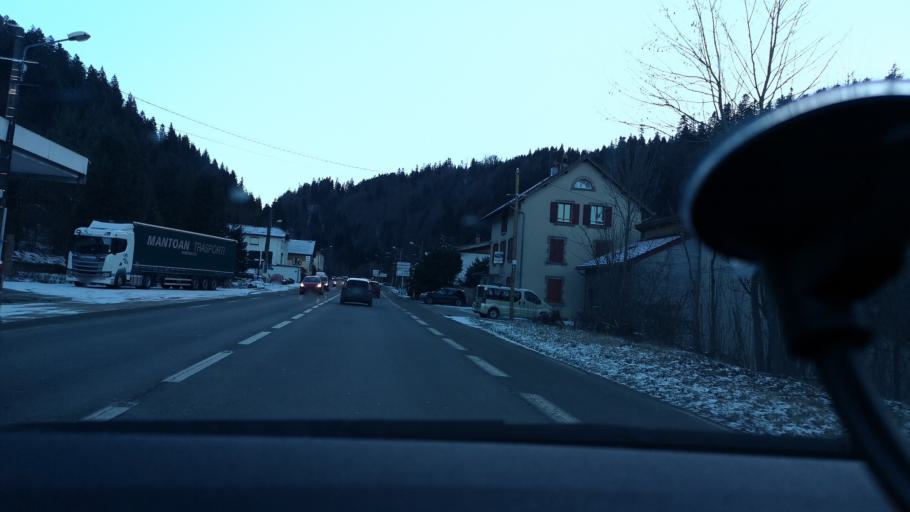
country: FR
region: Franche-Comte
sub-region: Departement du Doubs
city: La Cluse-et-Mijoux
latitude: 46.8862
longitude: 6.3651
